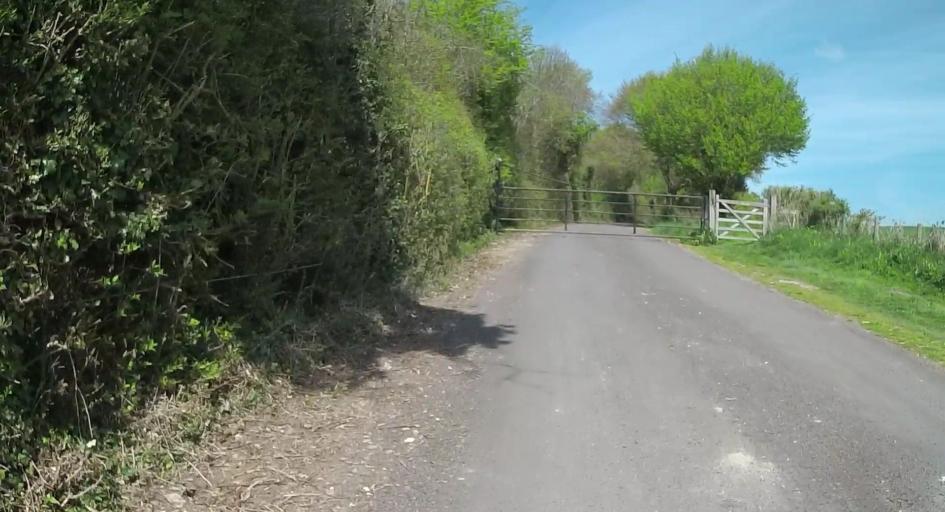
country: GB
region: England
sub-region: Hampshire
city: Chandlers Ford
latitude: 51.0967
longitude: -1.4148
